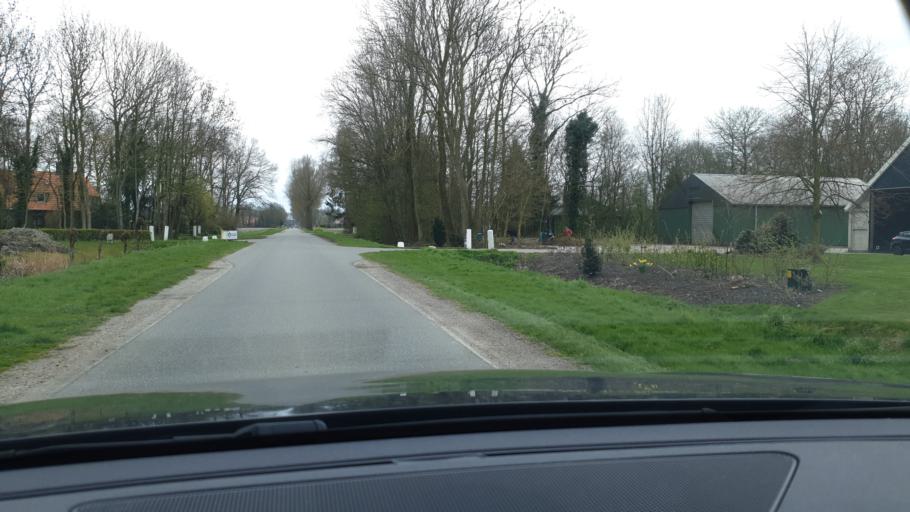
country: NL
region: Friesland
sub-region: Gemeente Lemsterland
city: Lemmer
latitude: 52.7827
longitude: 5.6632
